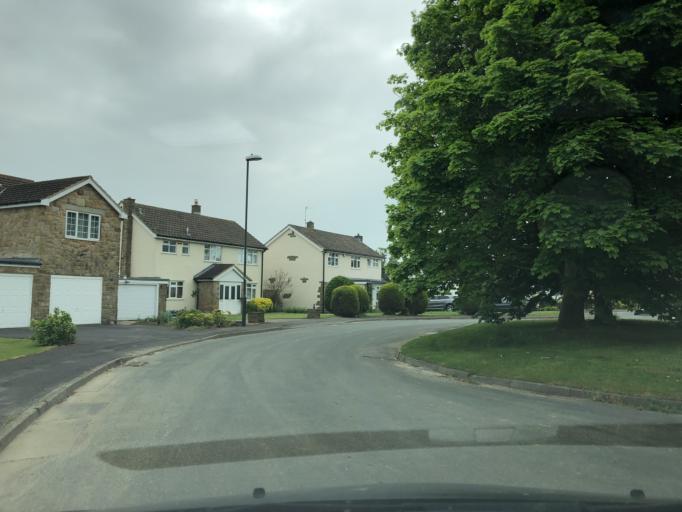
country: GB
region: England
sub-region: North Yorkshire
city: Harrogate
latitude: 54.0242
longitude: -1.5666
